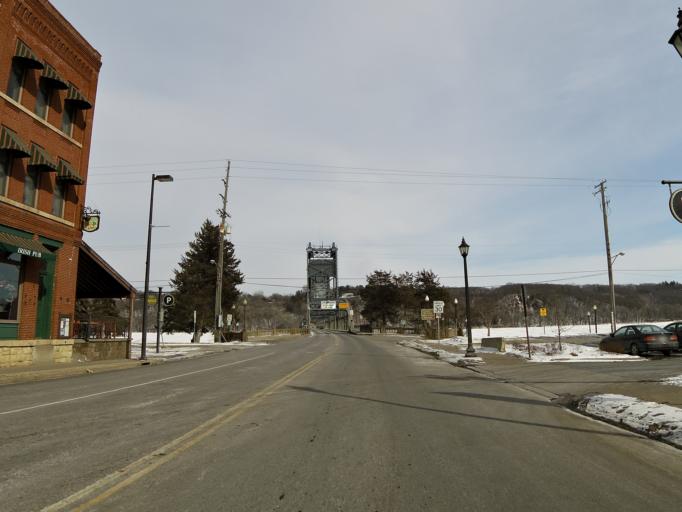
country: US
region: Minnesota
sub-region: Washington County
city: Stillwater
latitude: 45.0559
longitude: -92.8051
